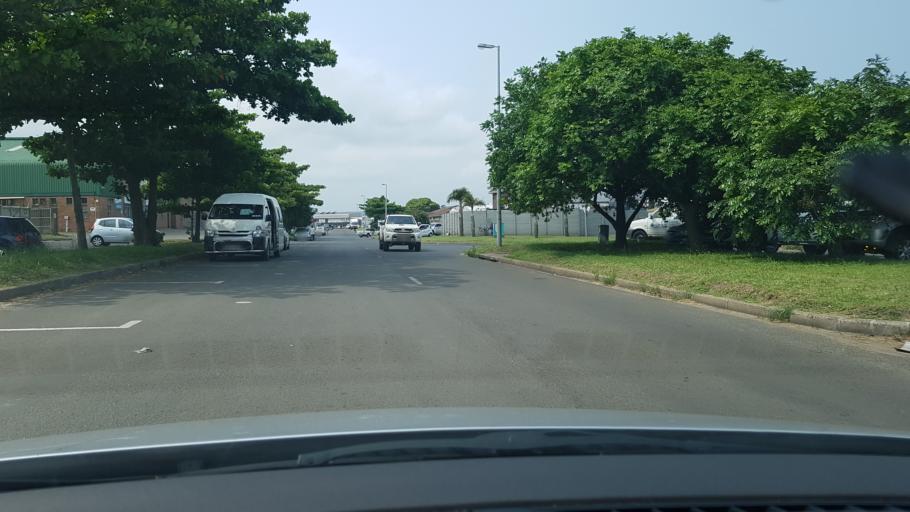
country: ZA
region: KwaZulu-Natal
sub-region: uThungulu District Municipality
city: Richards Bay
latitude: -28.7467
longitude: 32.0477
